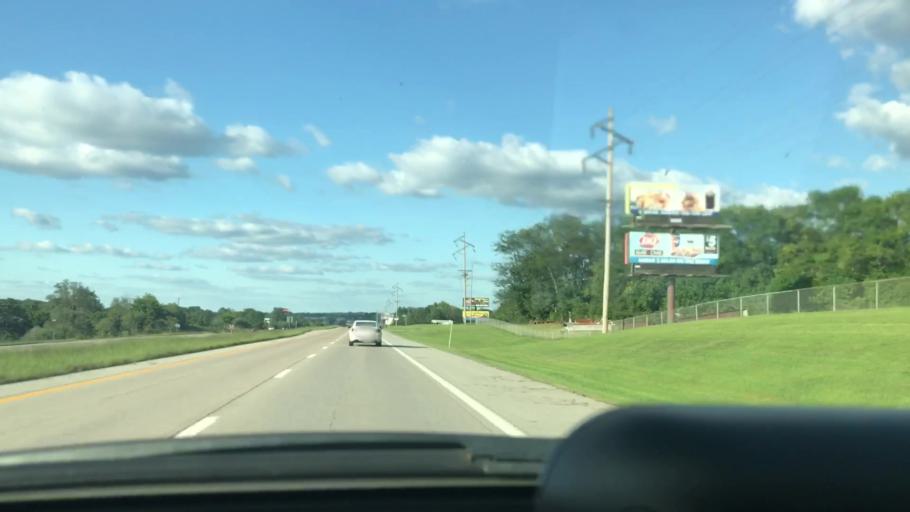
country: US
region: Missouri
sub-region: Pettis County
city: Sedalia
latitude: 38.6427
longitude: -93.2631
